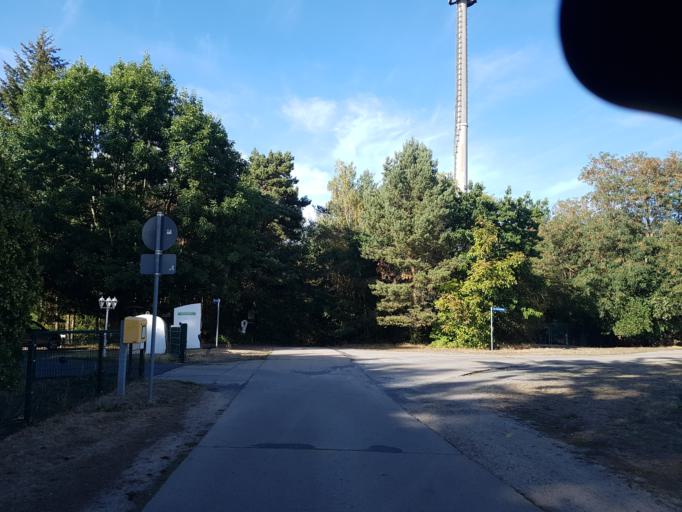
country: DE
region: Saxony-Anhalt
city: Jessen
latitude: 51.8059
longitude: 12.9891
